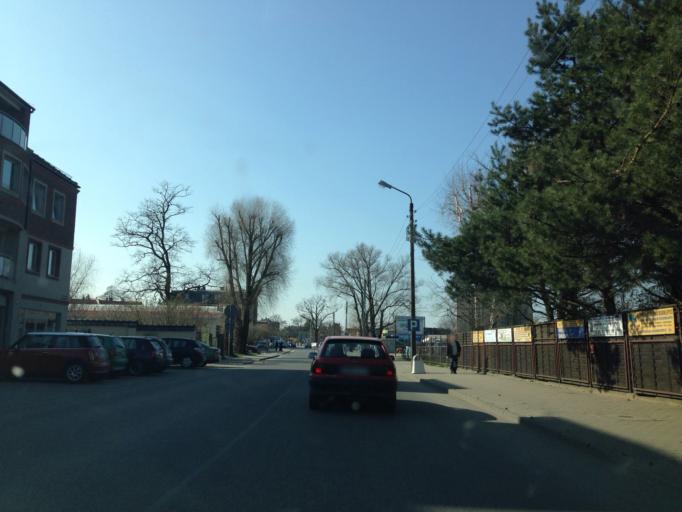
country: PL
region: Lower Silesian Voivodeship
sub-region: Powiat olesnicki
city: Olesnica
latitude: 51.2115
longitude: 17.3757
